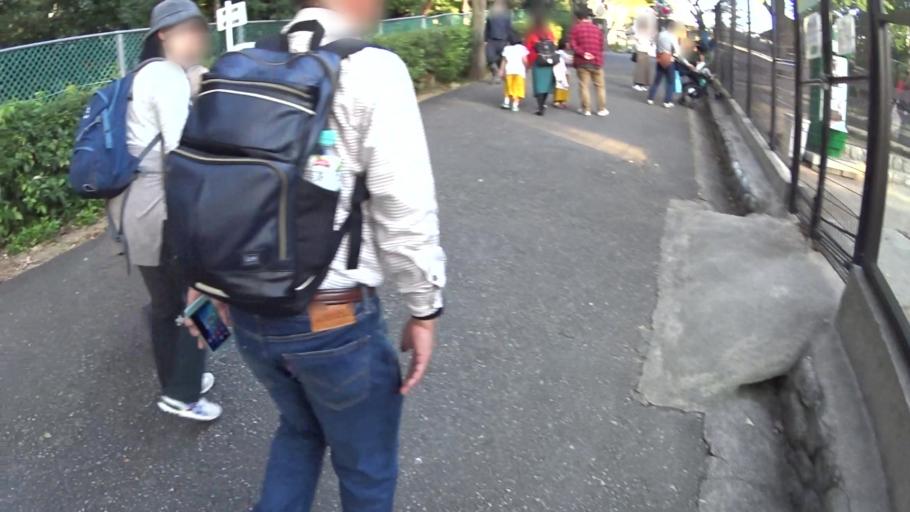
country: JP
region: Osaka
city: Ikeda
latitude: 34.8306
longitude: 135.4254
